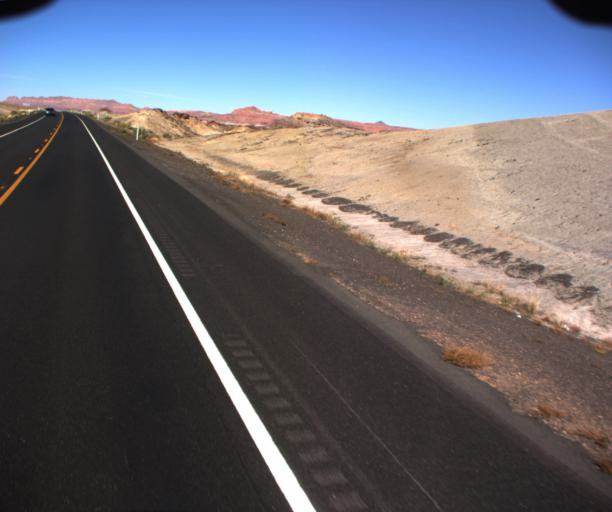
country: US
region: Arizona
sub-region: Coconino County
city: Tuba City
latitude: 36.1211
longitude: -111.3947
